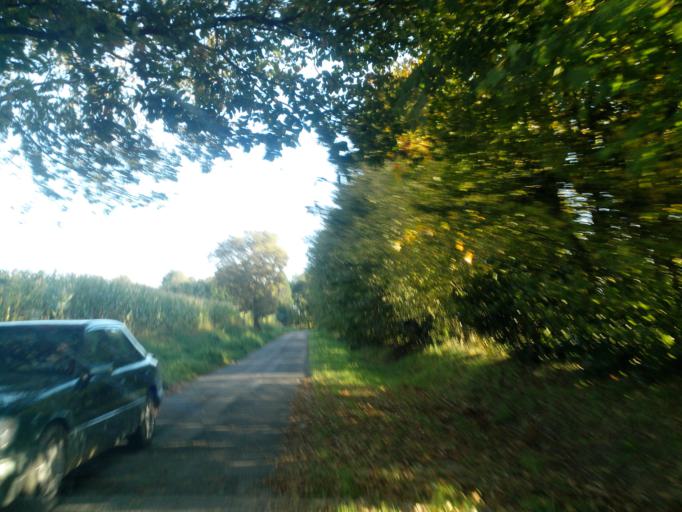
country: FR
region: Brittany
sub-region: Departement du Morbihan
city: Guilliers
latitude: 48.1111
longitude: -2.3650
